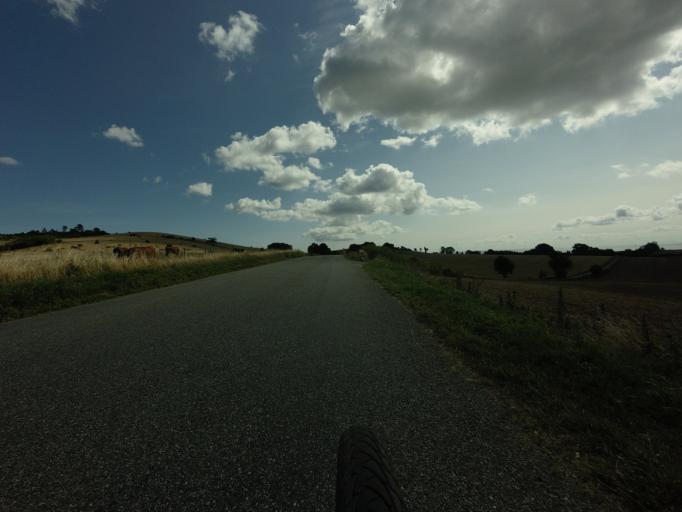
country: DK
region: Zealand
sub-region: Vordingborg Kommune
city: Stege
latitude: 54.9620
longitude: 12.5014
